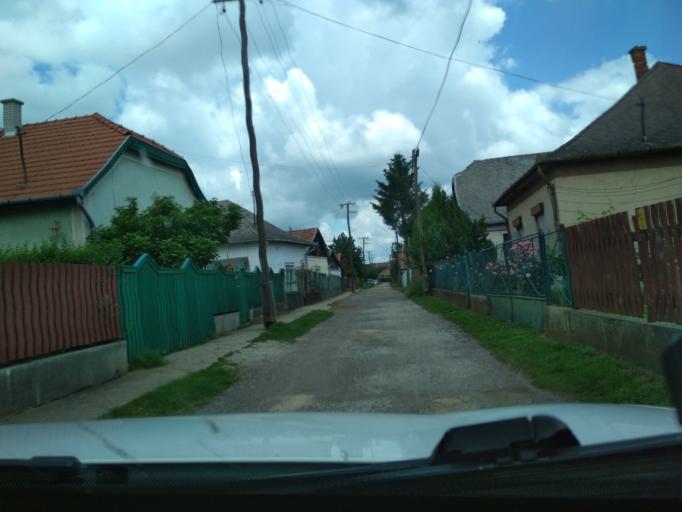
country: HU
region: Jasz-Nagykun-Szolnok
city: Tiszafured
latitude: 47.6043
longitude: 20.7716
